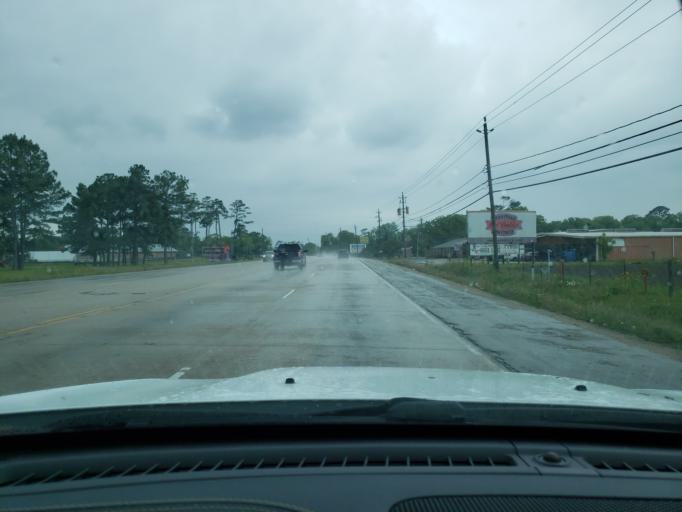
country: US
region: Texas
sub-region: Chambers County
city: Mont Belvieu
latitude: 29.7945
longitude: -94.9084
